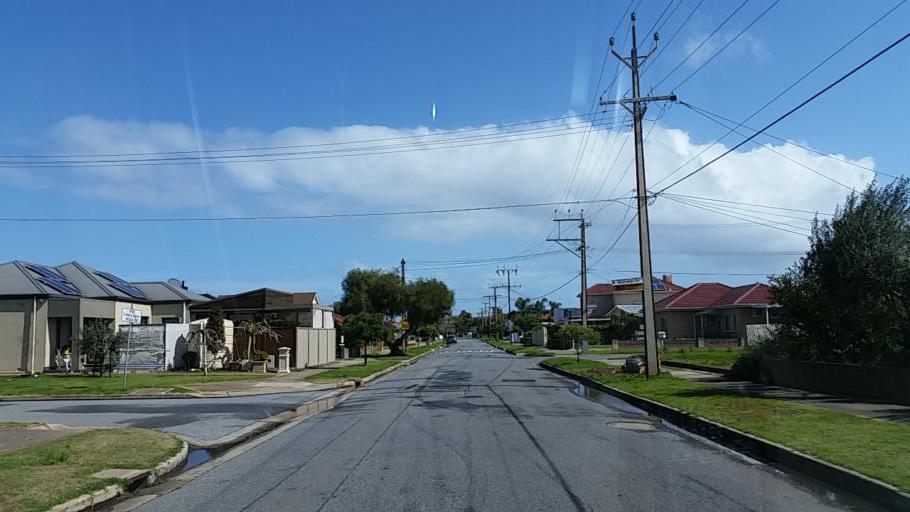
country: AU
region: South Australia
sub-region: Charles Sturt
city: Seaton
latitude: -34.9032
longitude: 138.5124
